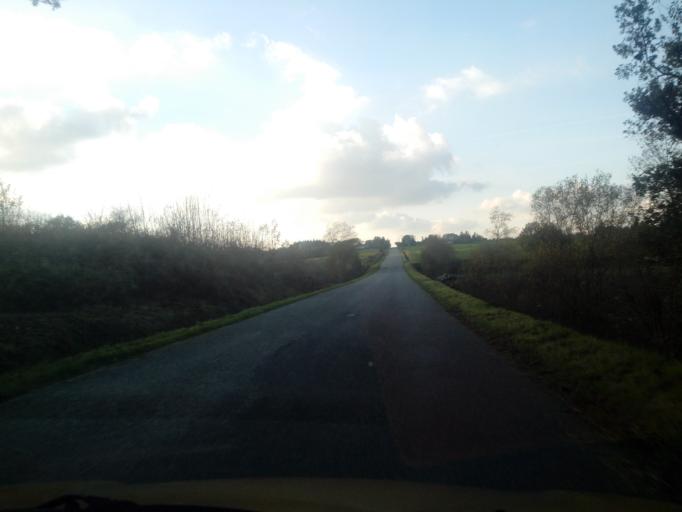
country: FR
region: Brittany
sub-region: Departement du Morbihan
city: Mauron
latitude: 48.0844
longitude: -2.3279
